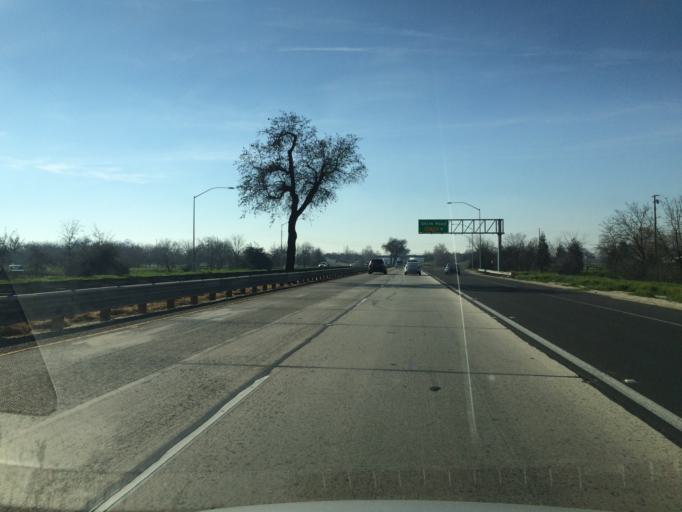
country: US
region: California
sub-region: Tulare County
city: Goshen
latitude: 36.3273
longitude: -119.3613
